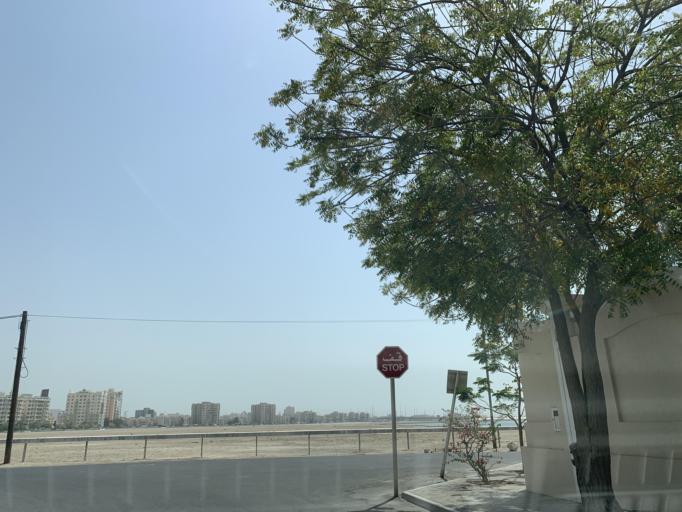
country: BH
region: Manama
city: Manama
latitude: 26.2014
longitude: 50.5763
